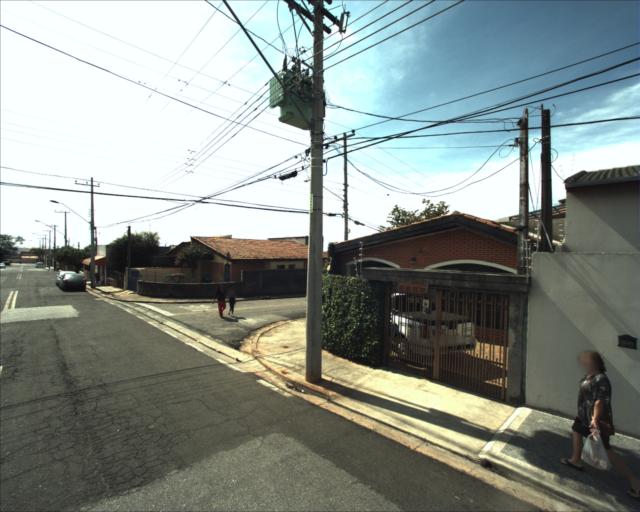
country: BR
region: Sao Paulo
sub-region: Sorocaba
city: Sorocaba
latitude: -23.5134
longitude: -47.5064
